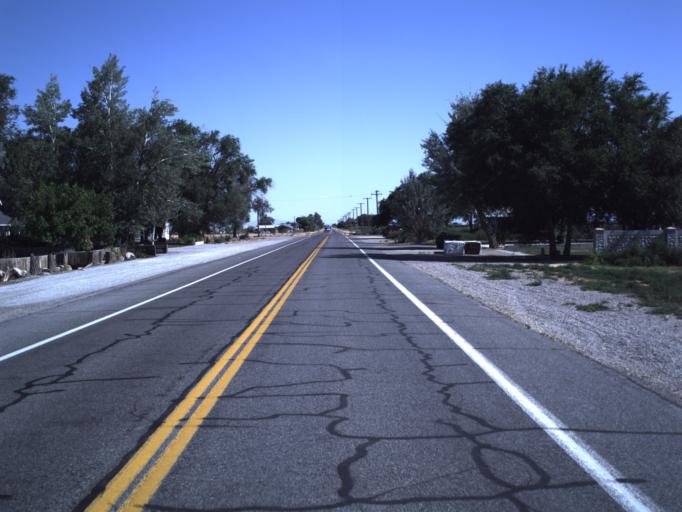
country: US
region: Utah
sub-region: Millard County
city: Delta
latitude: 39.2926
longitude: -112.6526
